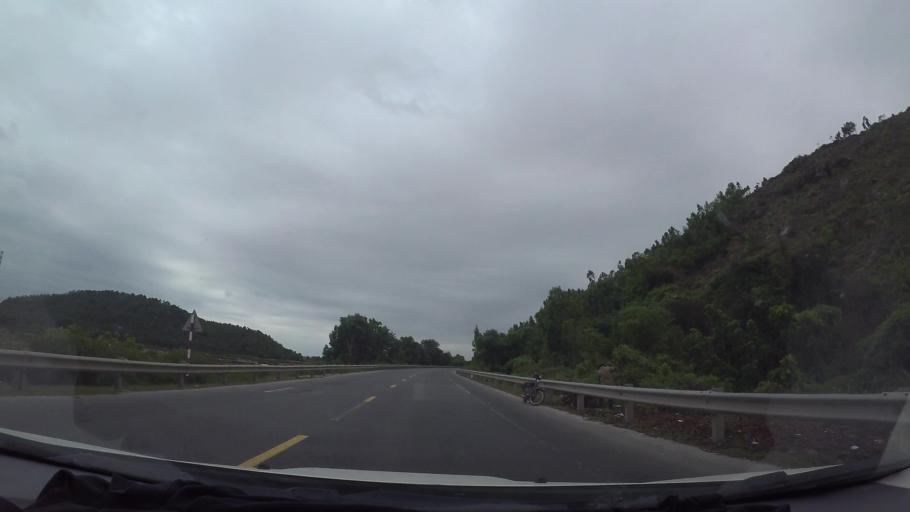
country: VN
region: Da Nang
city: Lien Chieu
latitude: 16.1203
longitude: 108.1024
